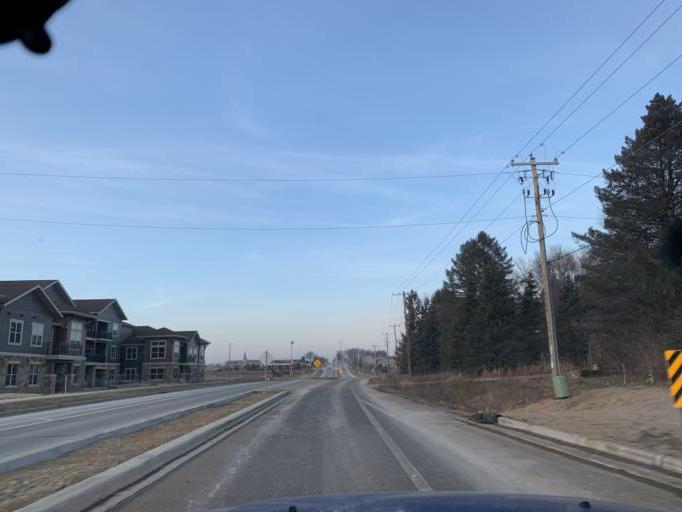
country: US
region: Wisconsin
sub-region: Dane County
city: Verona
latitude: 43.0519
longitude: -89.5522
